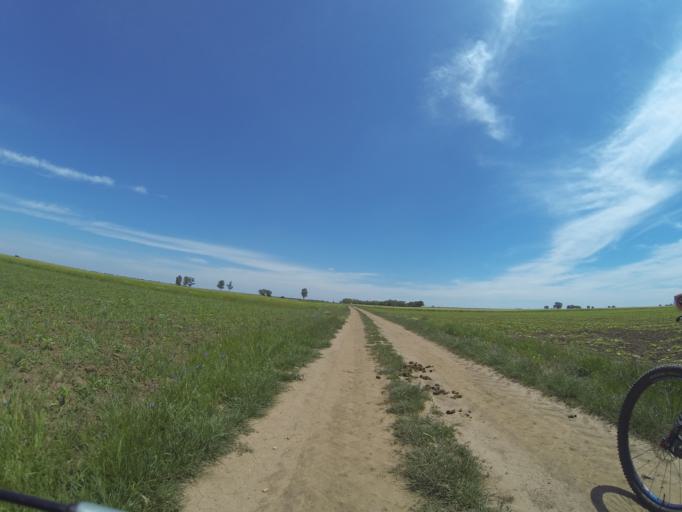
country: RO
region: Dolj
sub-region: Comuna Diosti
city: Radomir
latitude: 44.1464
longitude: 24.1584
